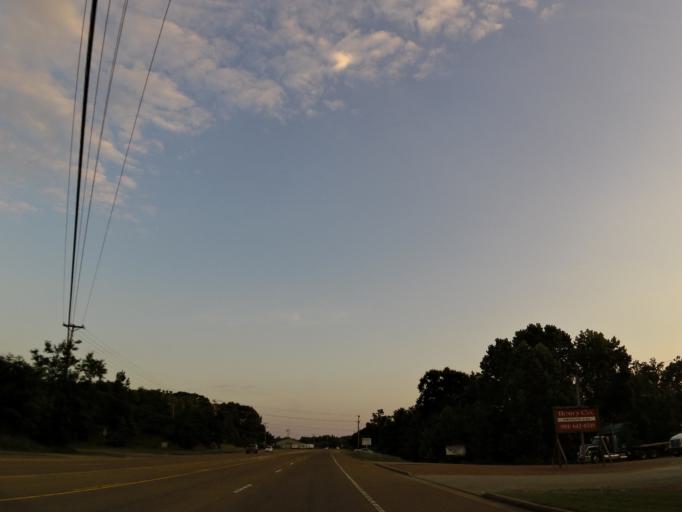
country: US
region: Tennessee
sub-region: Henry County
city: Paris
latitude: 36.2836
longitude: -88.3238
